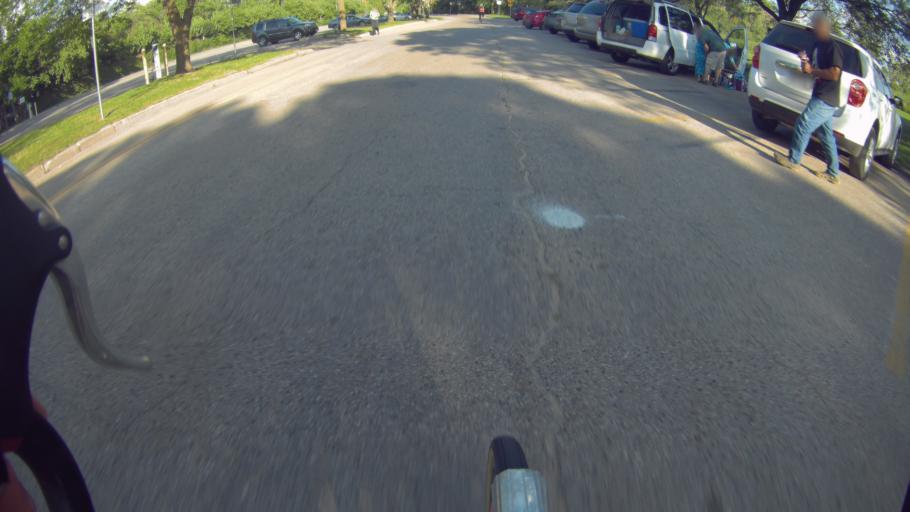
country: US
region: Wisconsin
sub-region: Dane County
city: Madison
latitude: 43.0582
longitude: -89.4105
